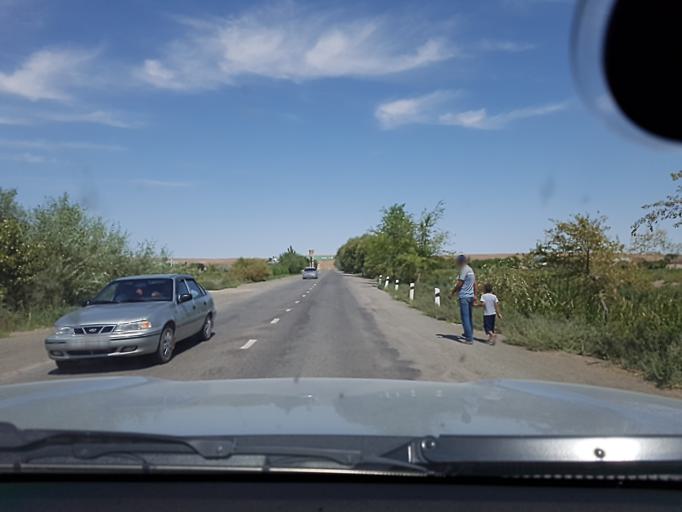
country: UZ
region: Karakalpakstan
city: Mang'it Shahri
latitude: 42.2412
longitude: 60.1471
